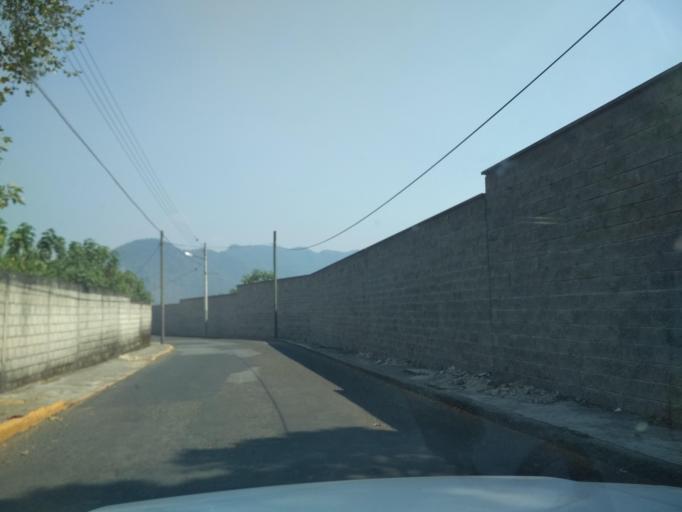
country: MX
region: Veracruz
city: Orizaba
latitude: 18.8444
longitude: -97.0895
